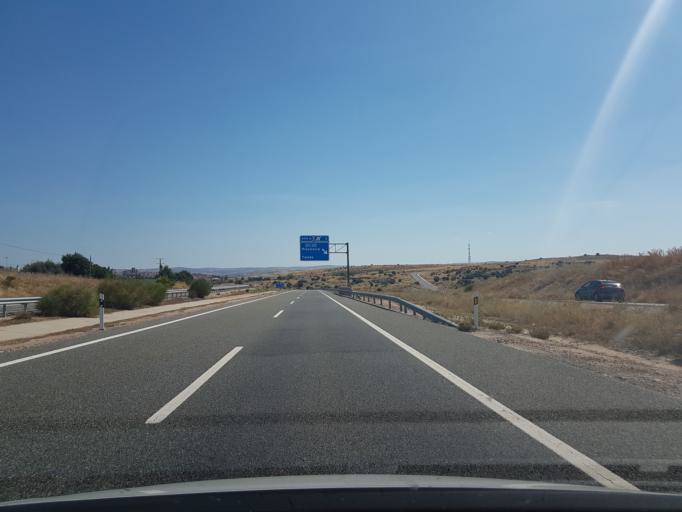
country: ES
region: Castille and Leon
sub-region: Provincia de Avila
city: Avila
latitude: 40.6747
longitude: -4.7277
